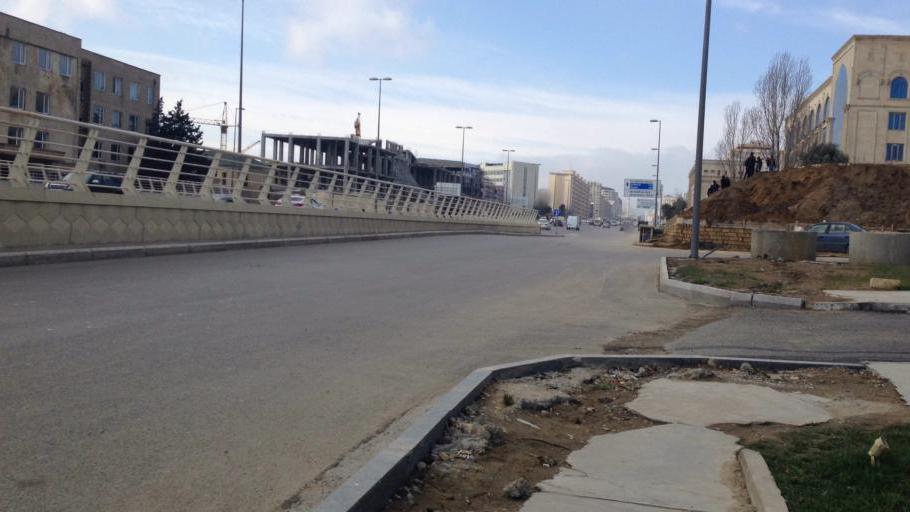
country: AZ
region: Baki
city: Baku
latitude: 40.4154
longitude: 49.8559
